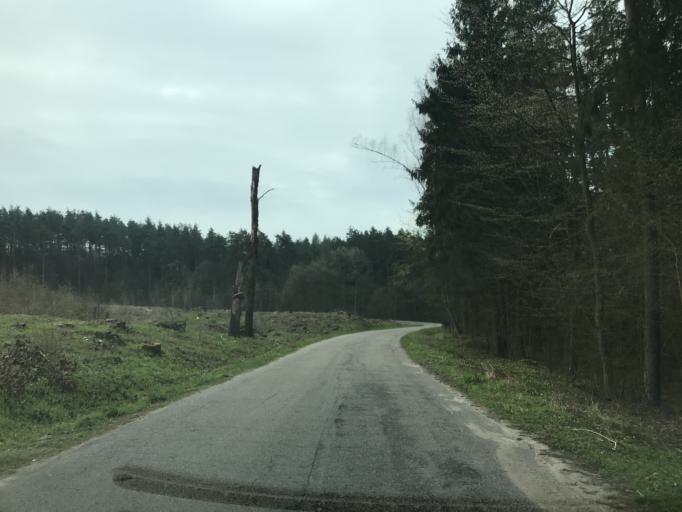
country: PL
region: Warmian-Masurian Voivodeship
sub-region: Powiat ostrodzki
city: Gierzwald
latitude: 53.6311
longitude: 20.1329
